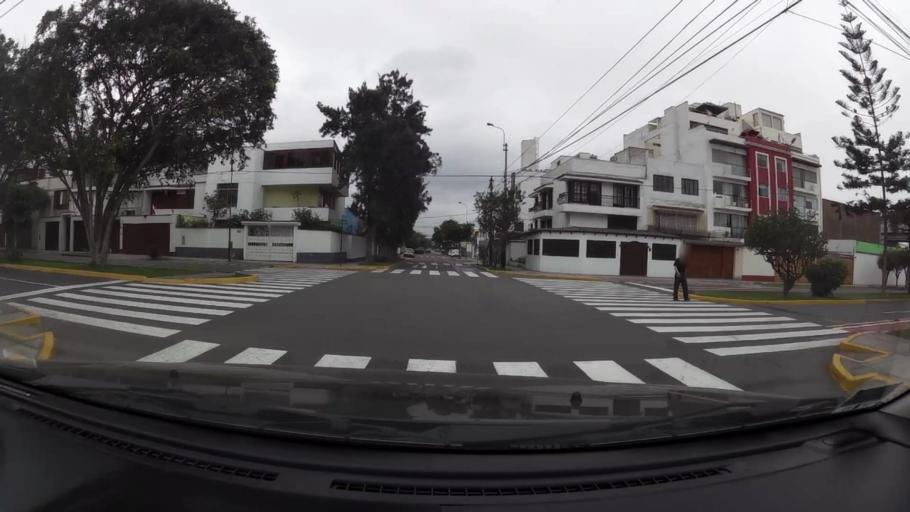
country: PE
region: Lima
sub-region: Lima
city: Surco
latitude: -12.1313
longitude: -76.9984
